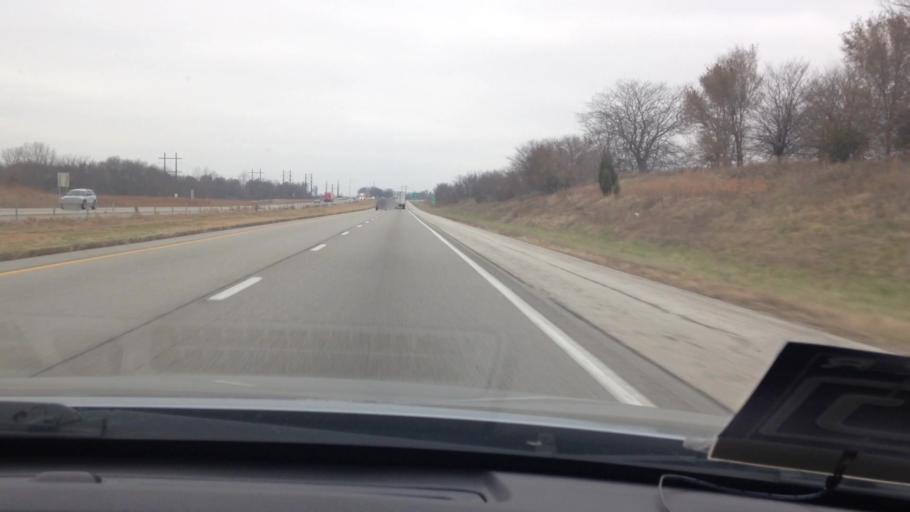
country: US
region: Missouri
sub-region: Cass County
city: Raymore
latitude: 38.7754
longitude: -94.4937
